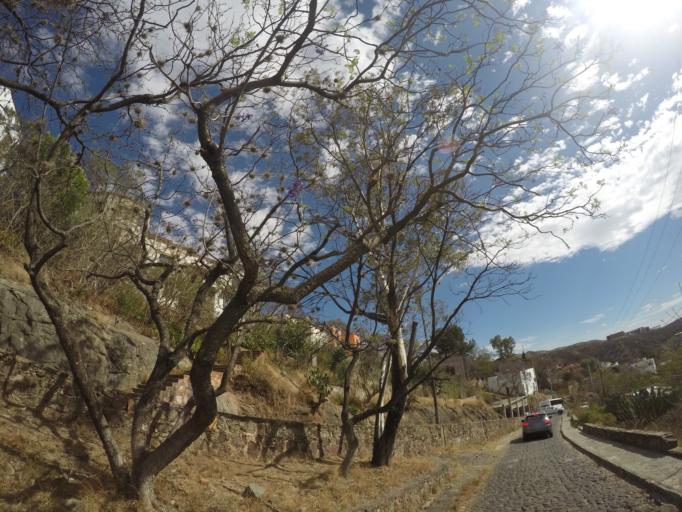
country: MX
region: Guanajuato
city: Guanajuato
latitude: 21.0143
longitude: -101.2638
